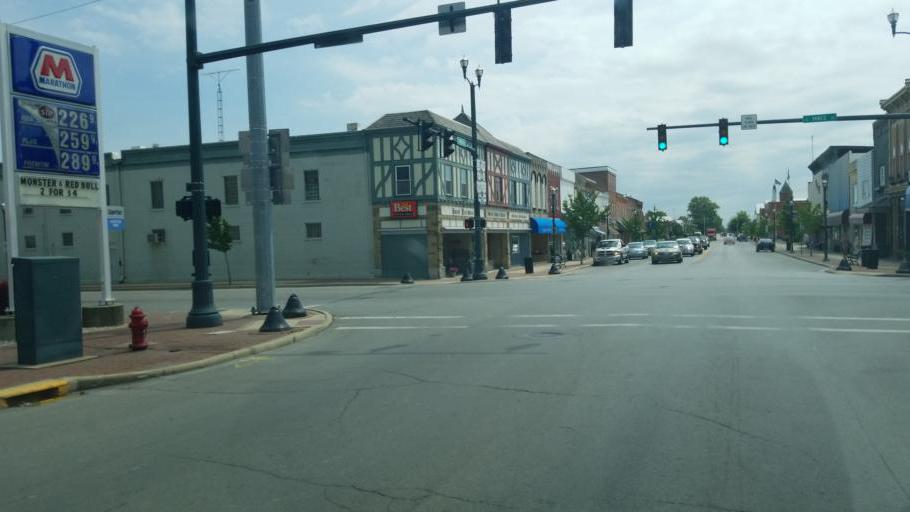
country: US
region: Ohio
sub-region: Wyandot County
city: Carey
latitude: 40.9526
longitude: -83.3830
